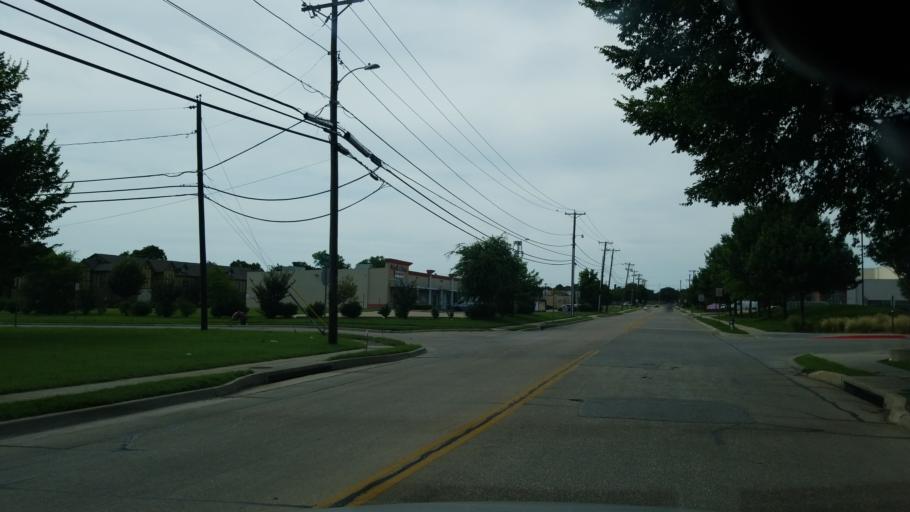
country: US
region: Texas
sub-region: Dallas County
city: Irving
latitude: 32.8329
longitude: -96.9445
